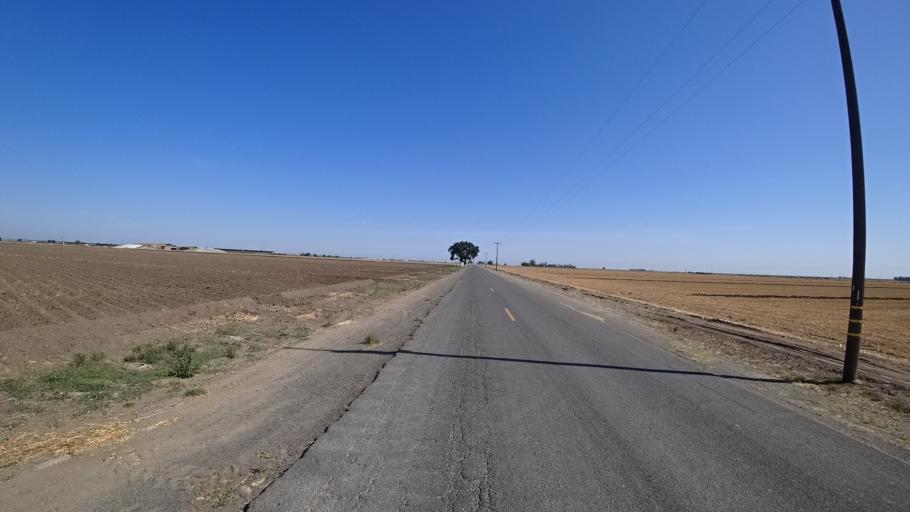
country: US
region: California
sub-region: Kings County
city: Corcoran
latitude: 36.2163
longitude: -119.5470
